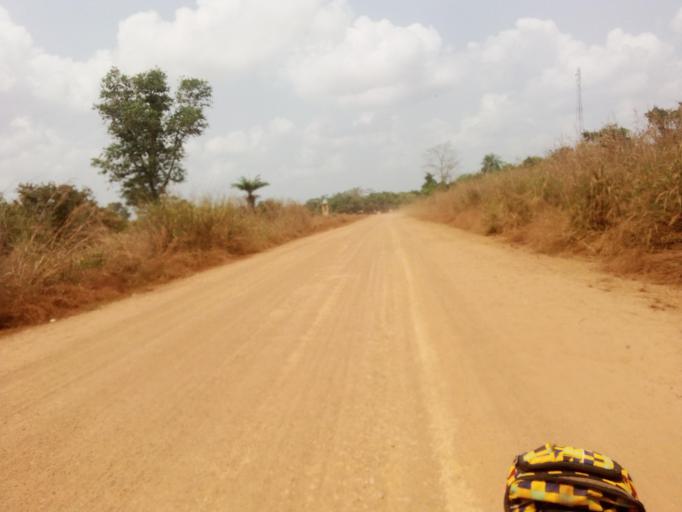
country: SL
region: Southern Province
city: Mogbwemo
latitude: 7.6638
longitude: -12.2724
